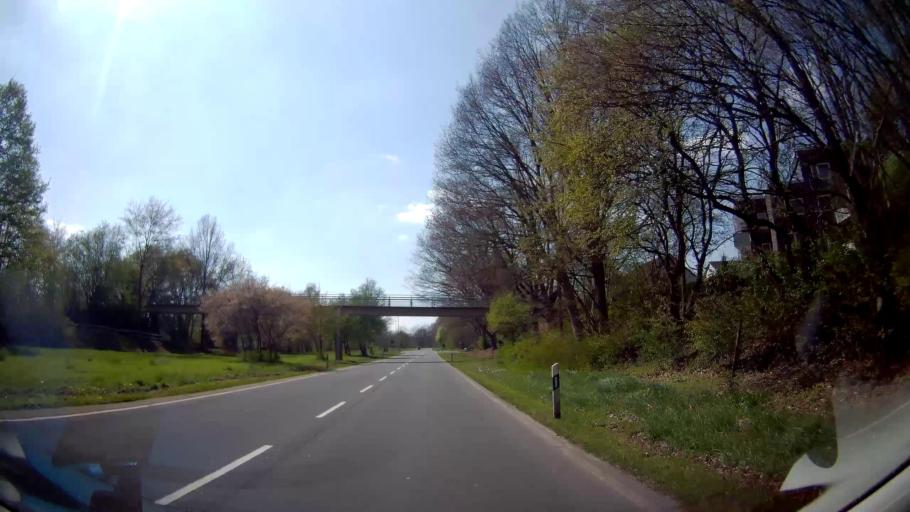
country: DE
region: North Rhine-Westphalia
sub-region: Regierungsbezirk Munster
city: Klein Reken
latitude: 51.7270
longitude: 7.0453
